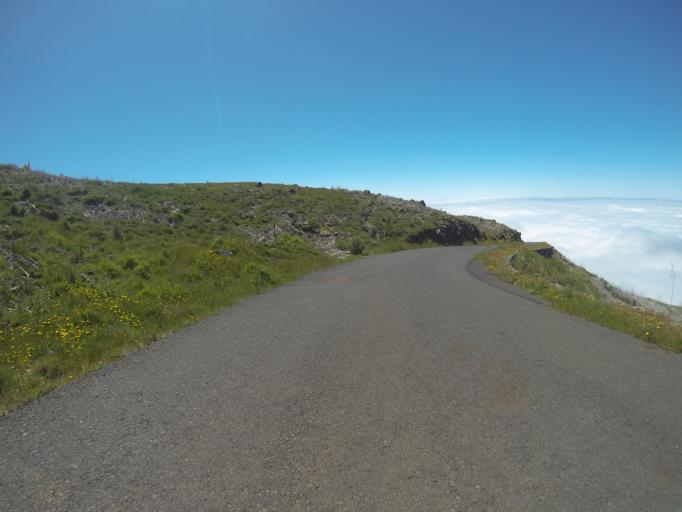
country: PT
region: Madeira
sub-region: Funchal
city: Nossa Senhora do Monte
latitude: 32.7059
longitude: -16.9147
